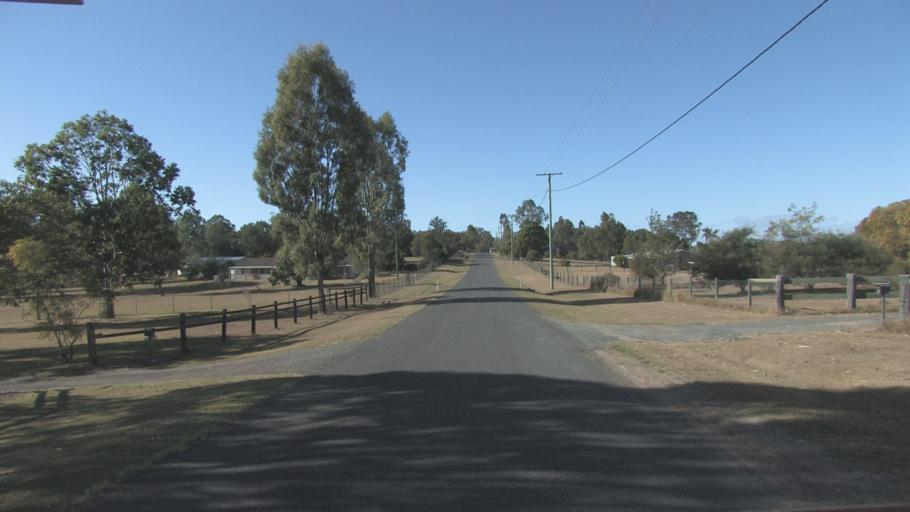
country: AU
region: Queensland
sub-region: Logan
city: Cedar Vale
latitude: -27.8338
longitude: 152.9910
